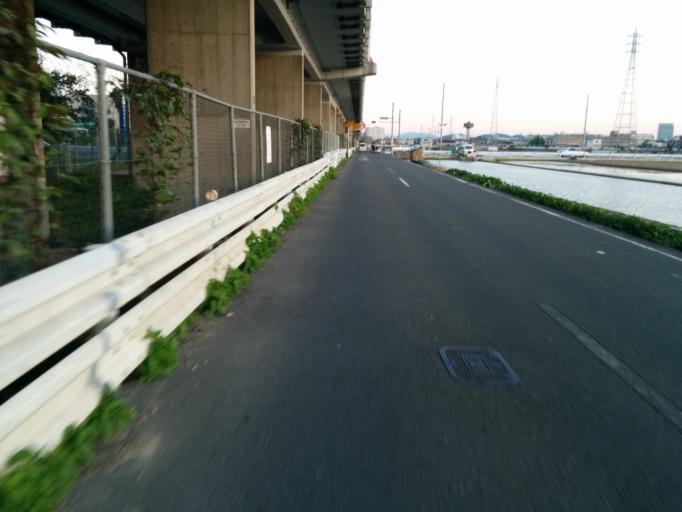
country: JP
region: Kyoto
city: Muko
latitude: 34.9438
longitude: 135.7145
